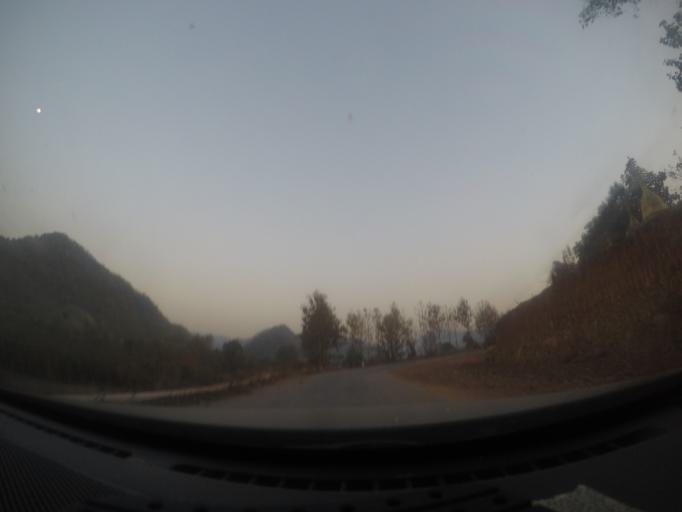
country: MM
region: Mandalay
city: Yamethin
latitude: 20.7371
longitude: 96.4903
